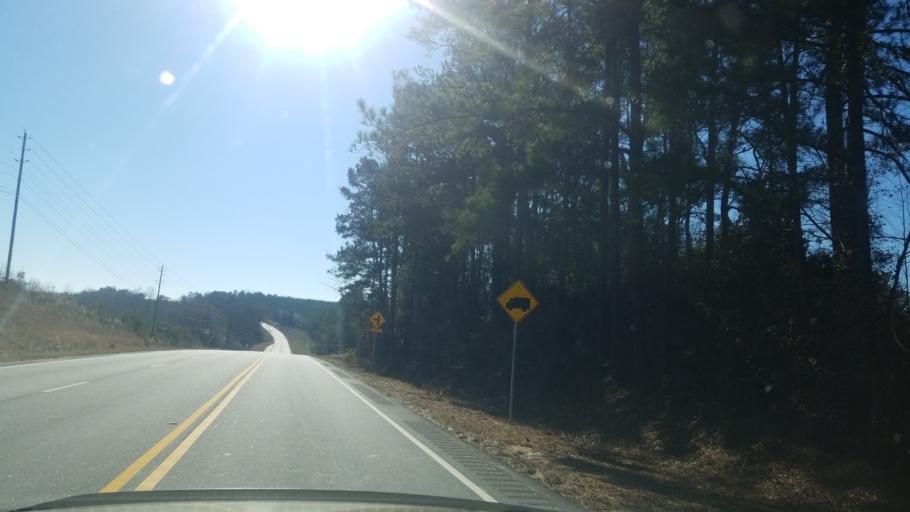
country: US
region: Alabama
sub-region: Chambers County
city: Valley
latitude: 32.8489
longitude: -85.1270
